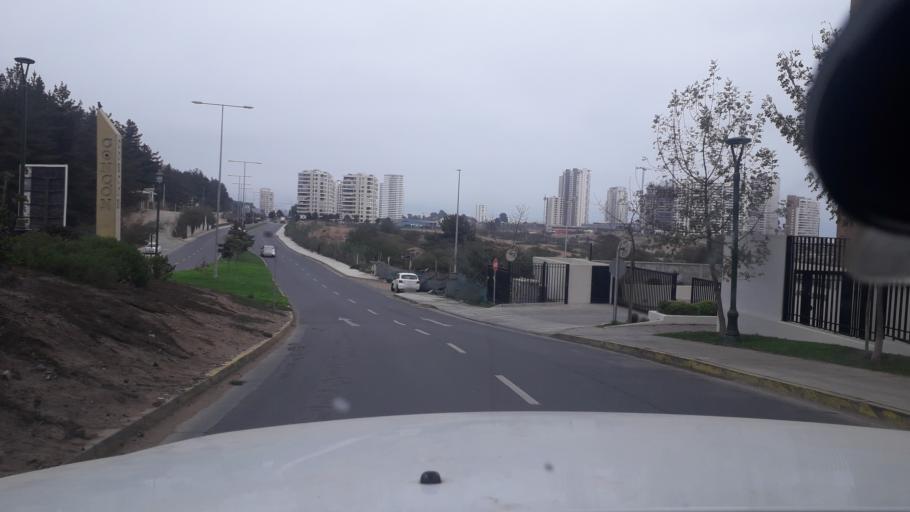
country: CL
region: Valparaiso
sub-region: Provincia de Valparaiso
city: Vina del Mar
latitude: -32.9508
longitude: -71.5387
